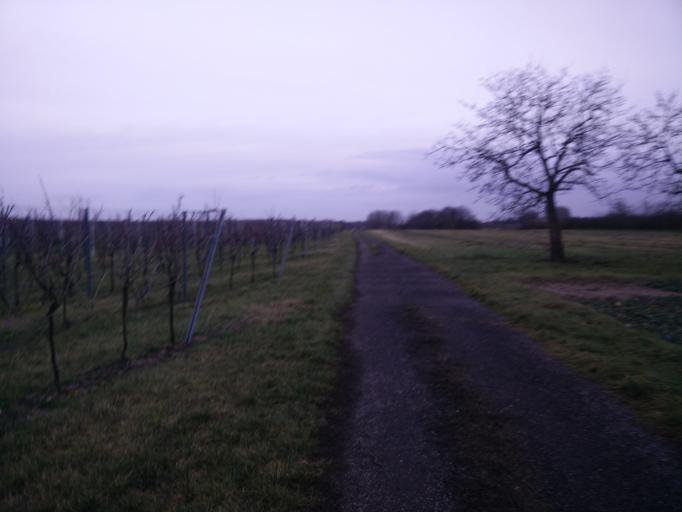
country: DE
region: Rheinland-Pfalz
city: Oberhausen
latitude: 49.1048
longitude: 8.0563
